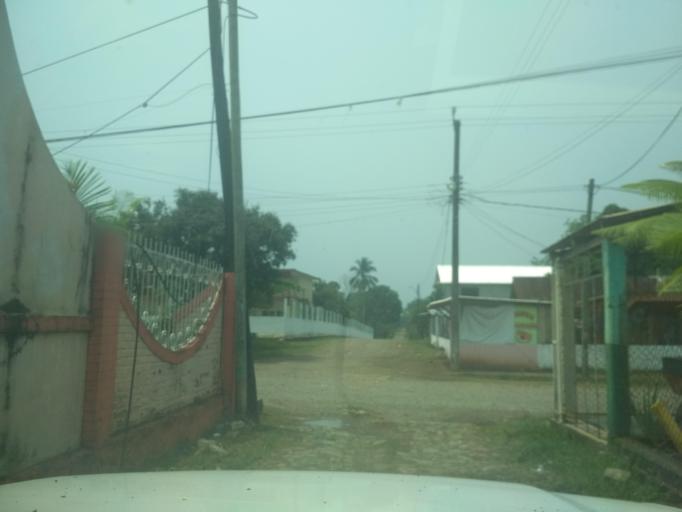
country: MX
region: Veracruz
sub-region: Tezonapa
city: Laguna Chica (Pueblo Nuevo)
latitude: 18.5163
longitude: -96.7792
